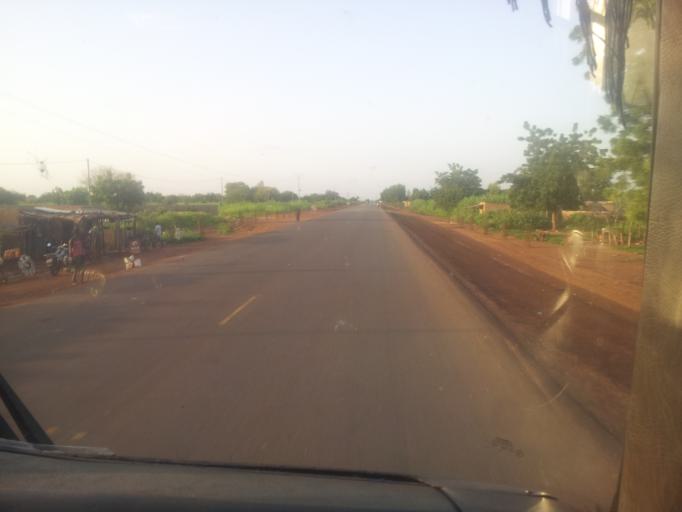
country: BF
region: Centre-Est
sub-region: Kouritenga Province
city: Koupela
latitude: 12.1434
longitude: -0.3710
